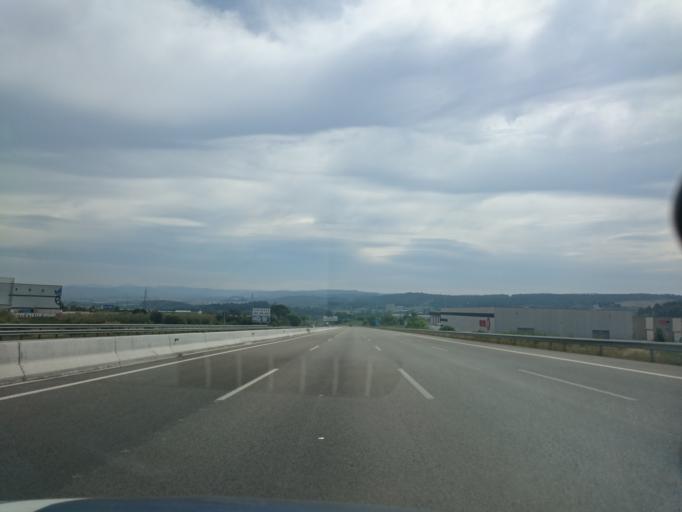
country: ES
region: Catalonia
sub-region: Provincia de Barcelona
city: Navarcles
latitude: 41.7795
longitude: 1.8923
